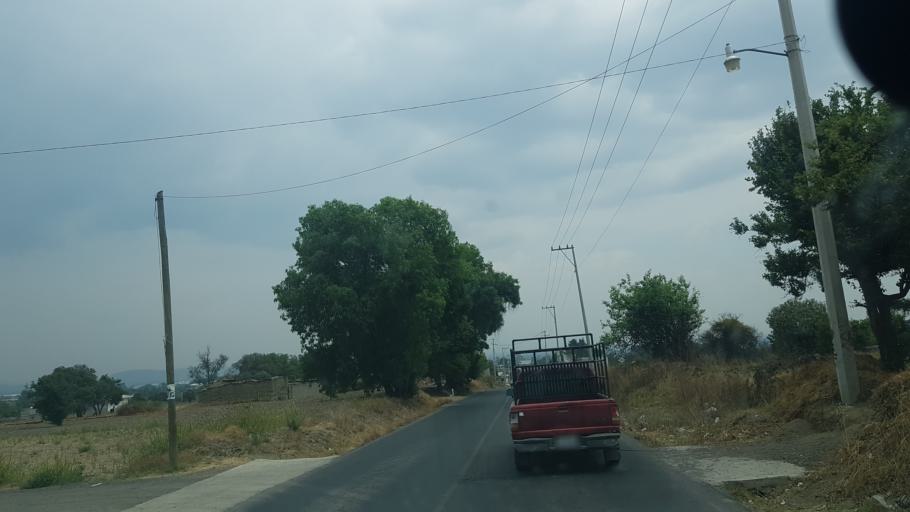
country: MX
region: Puebla
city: San Lorenzo Chiautzingo
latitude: 19.1976
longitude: -98.4478
